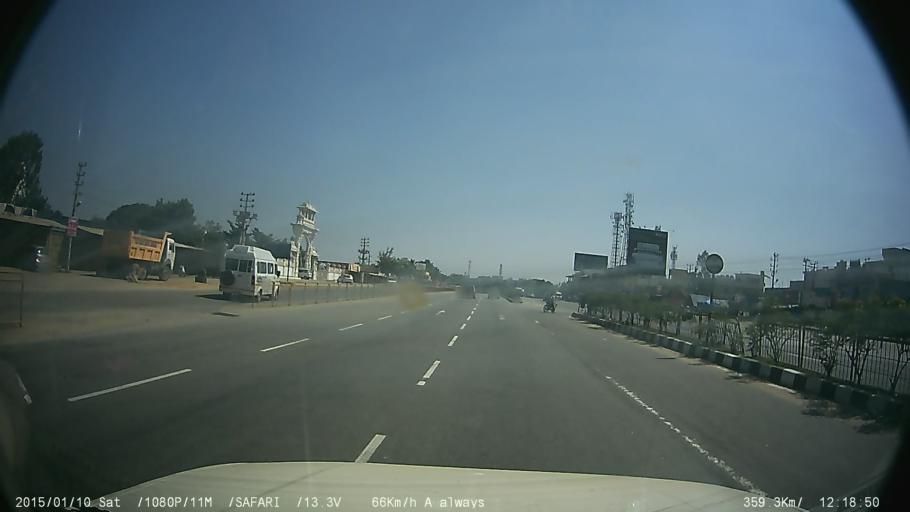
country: IN
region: Karnataka
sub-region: Bangalore Urban
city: Anekal
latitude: 12.7891
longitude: 77.7346
